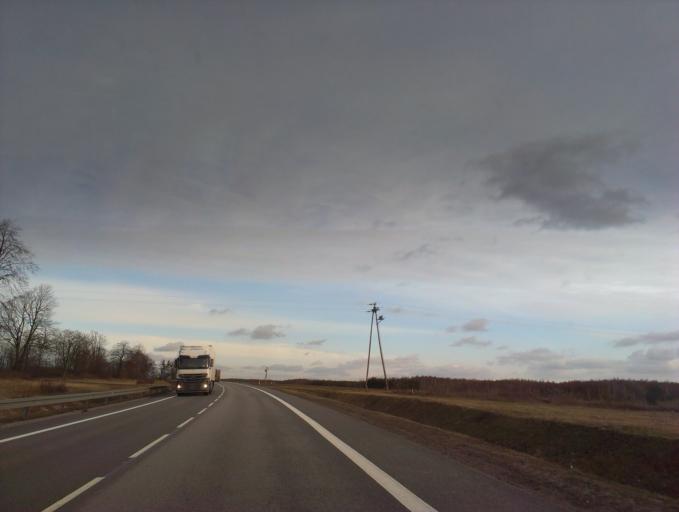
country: PL
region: Kujawsko-Pomorskie
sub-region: Powiat lipnowski
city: Skepe
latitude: 52.8571
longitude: 19.2975
